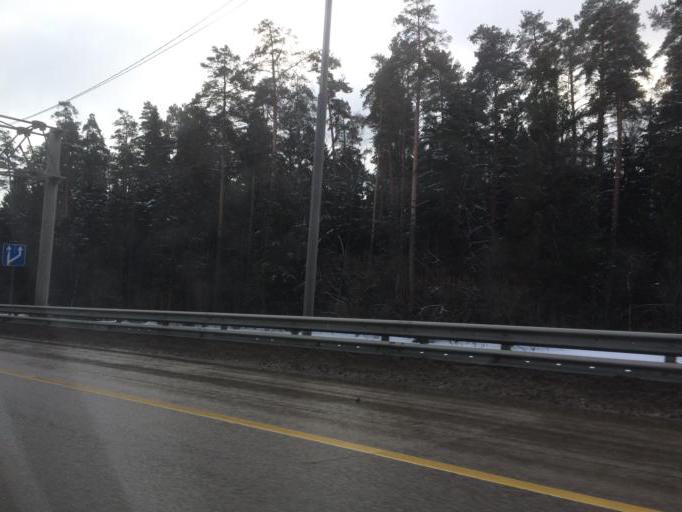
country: RU
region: Moskovskaya
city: Petrovo-Dal'neye
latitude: 55.7784
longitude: 37.1820
